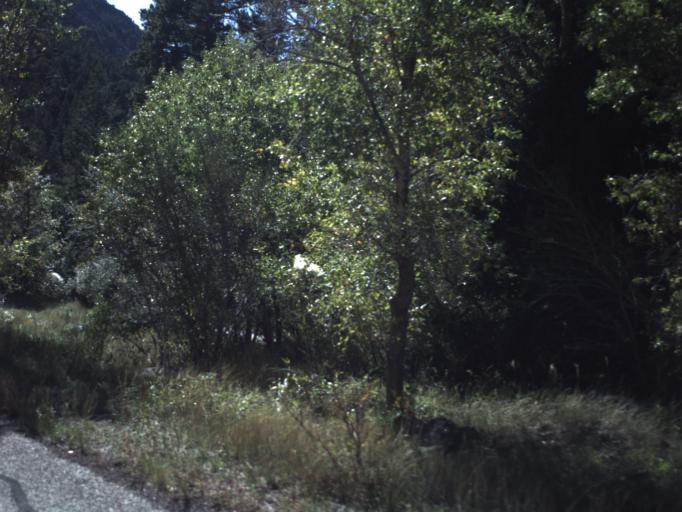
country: US
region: Utah
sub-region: Beaver County
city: Beaver
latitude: 38.2577
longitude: -112.5224
